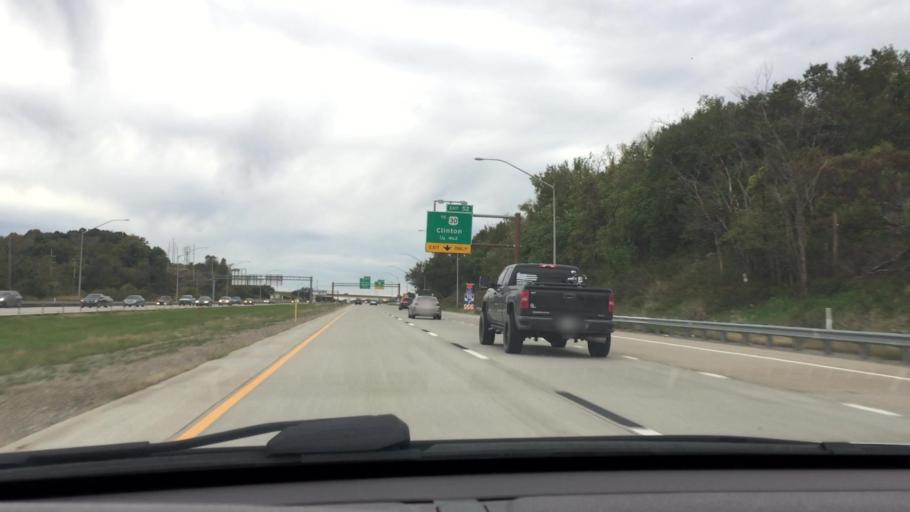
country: US
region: Pennsylvania
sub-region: Allegheny County
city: Imperial
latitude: 40.4930
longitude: -80.2743
